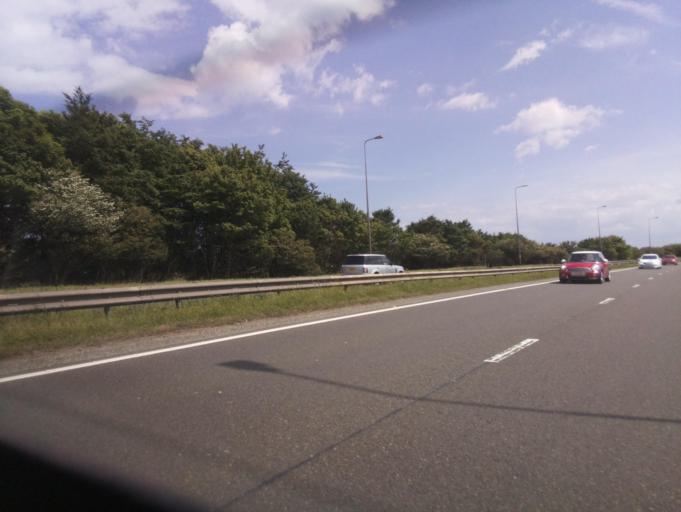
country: GB
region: England
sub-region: County Durham
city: Peterlee
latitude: 54.7245
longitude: -1.3343
